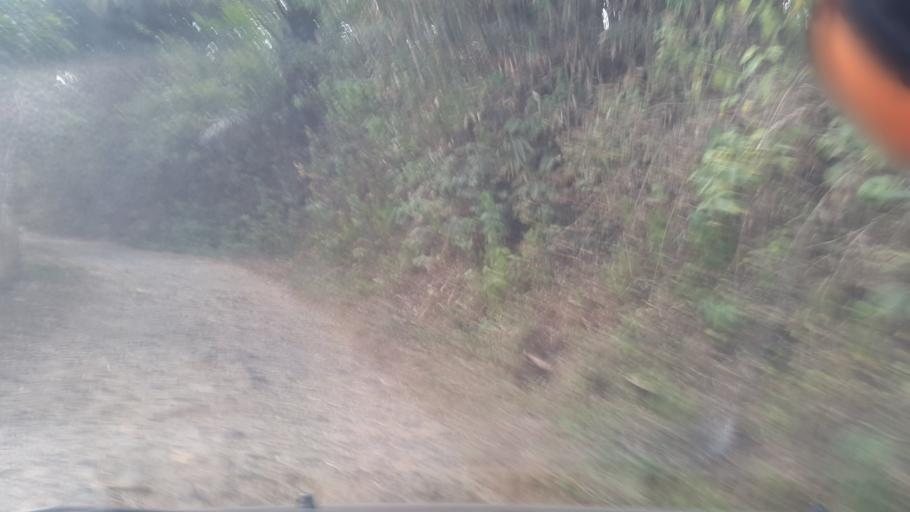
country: ID
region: West Java
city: Nangerang
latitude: -7.1148
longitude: 106.7916
